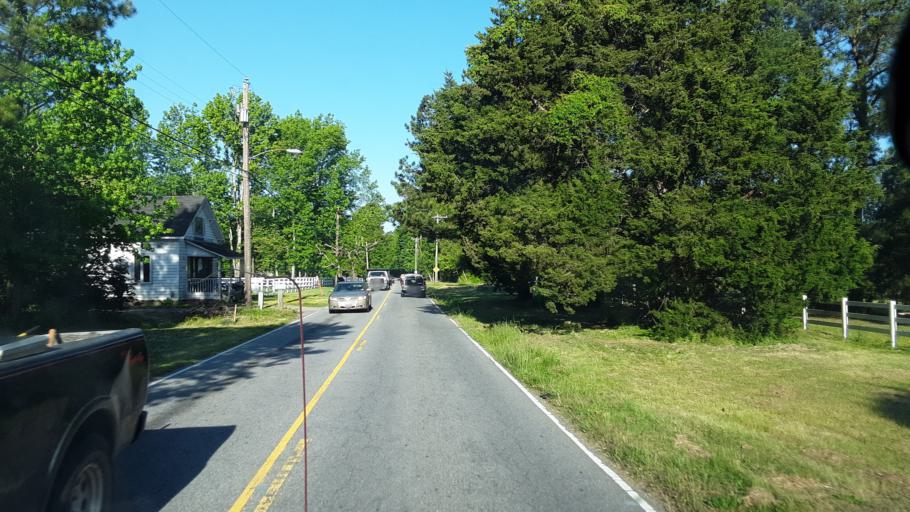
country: US
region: Virginia
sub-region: City of Virginia Beach
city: Virginia Beach
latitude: 36.7236
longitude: -76.0189
